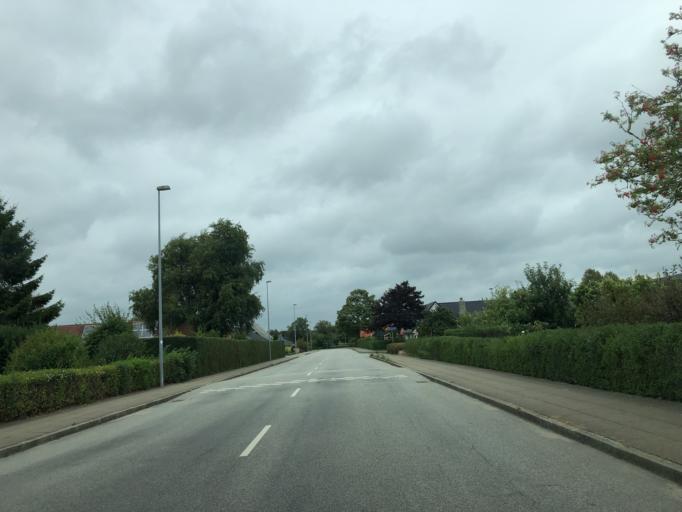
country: DK
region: Central Jutland
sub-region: Herning Kommune
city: Snejbjerg
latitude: 56.1293
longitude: 8.8987
